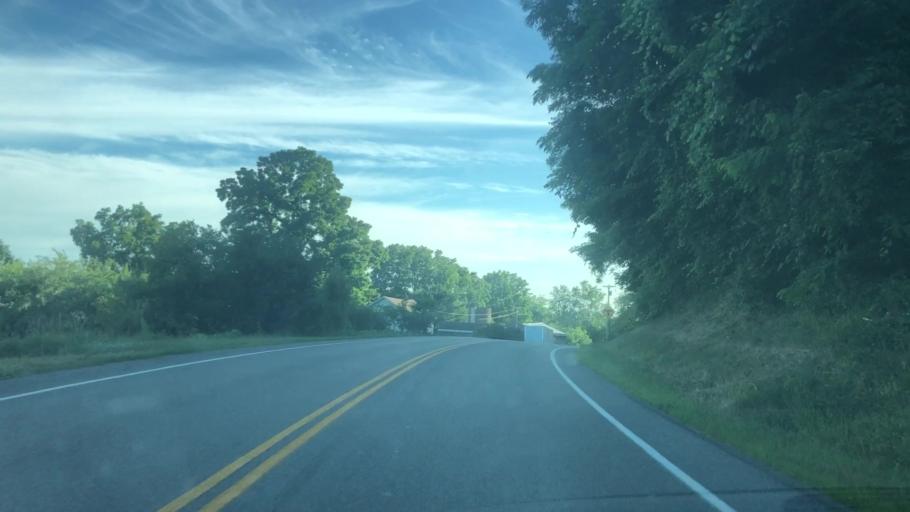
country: US
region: New York
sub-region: Ontario County
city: Victor
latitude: 43.0265
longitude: -77.4328
